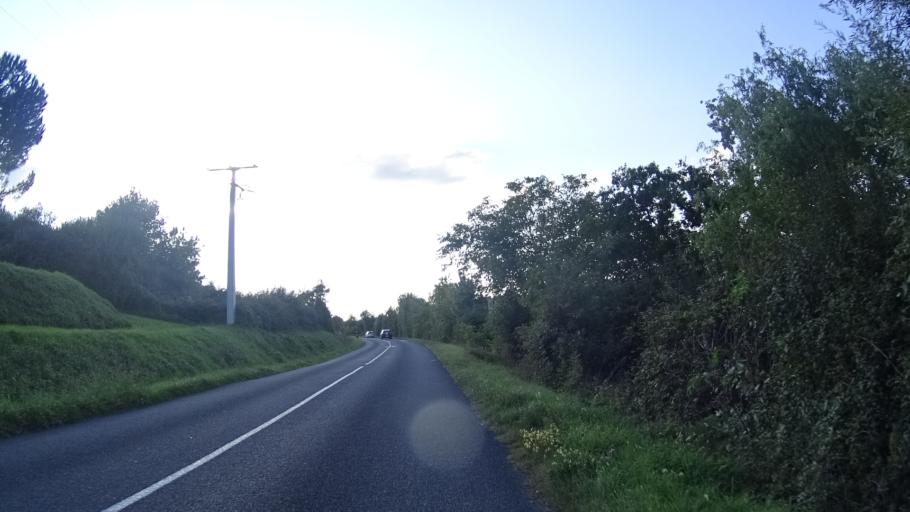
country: FR
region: Pays de la Loire
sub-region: Departement de Maine-et-Loire
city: Drain
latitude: 47.3451
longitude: -1.1886
